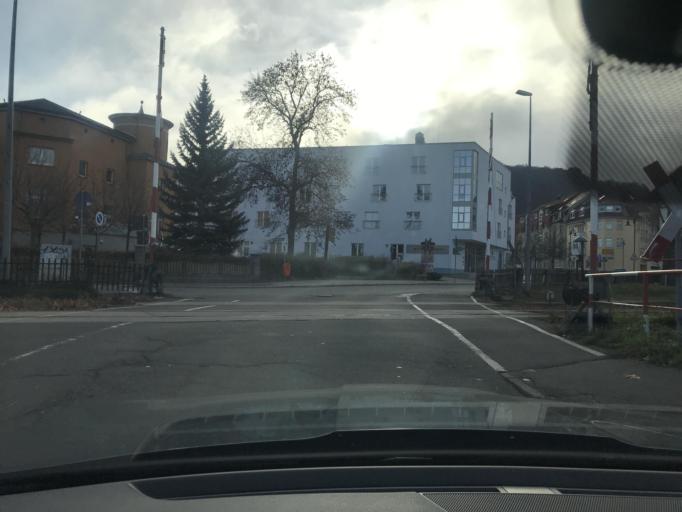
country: DE
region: Saxony-Anhalt
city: Thale
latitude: 51.7473
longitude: 11.0334
